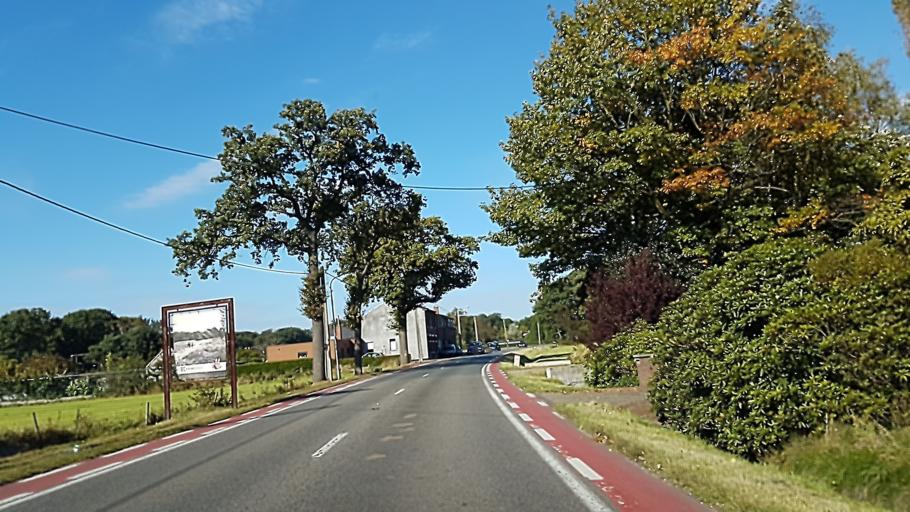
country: BE
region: Flanders
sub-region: Provincie Antwerpen
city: Kalmthout
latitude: 51.4025
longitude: 4.4680
